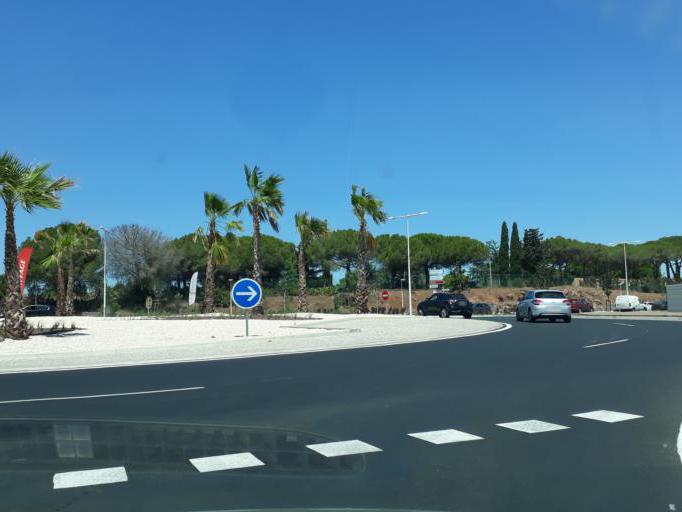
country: FR
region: Languedoc-Roussillon
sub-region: Departement de l'Herault
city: Le Cap d'Agde
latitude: 43.2886
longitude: 3.5077
